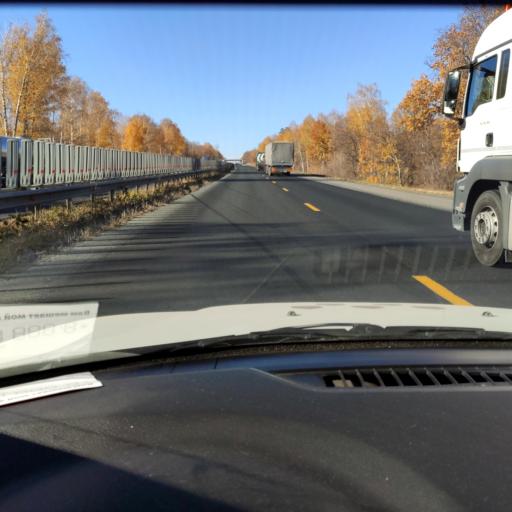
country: RU
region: Samara
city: Bogatyr'
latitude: 53.5114
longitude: 49.9449
